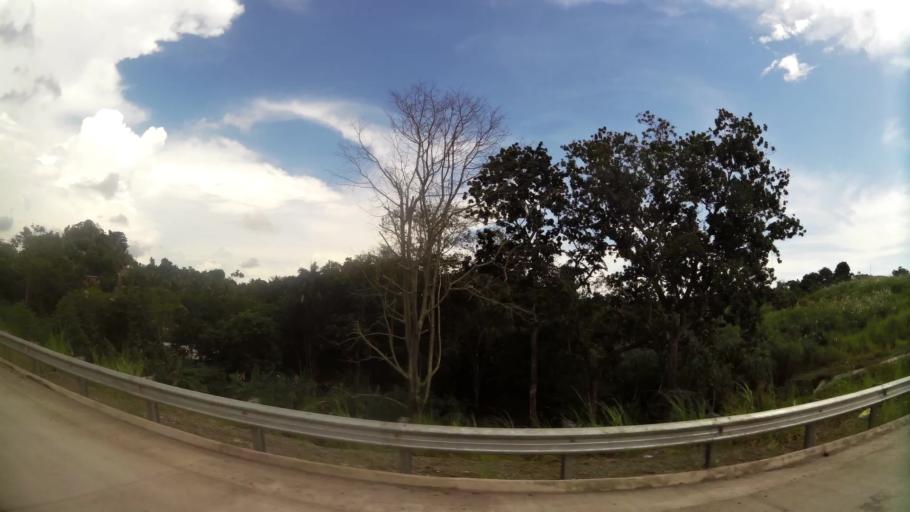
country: PA
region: Panama
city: San Miguelito
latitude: 9.0893
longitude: -79.4414
